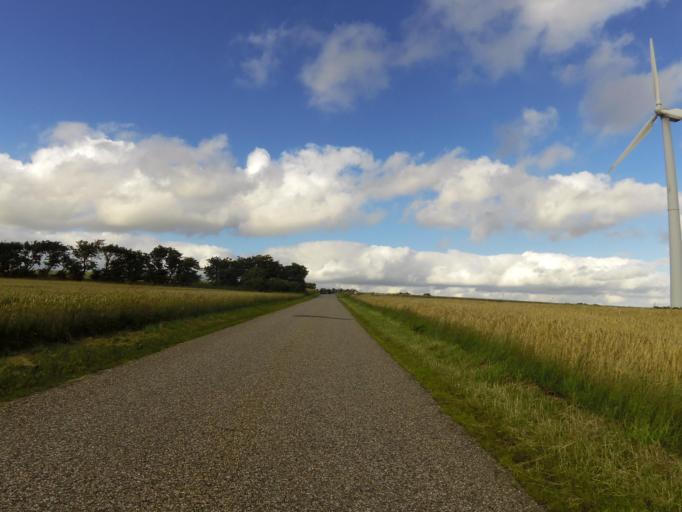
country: DK
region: South Denmark
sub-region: Tonder Kommune
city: Toftlund
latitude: 55.1414
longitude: 9.0809
